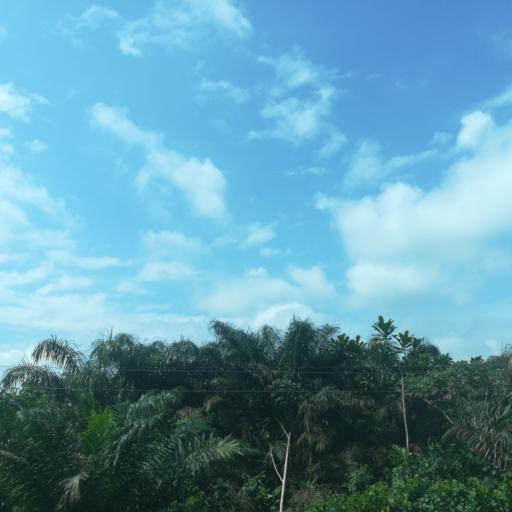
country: NG
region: Lagos
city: Ikorodu
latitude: 6.6560
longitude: 3.6900
